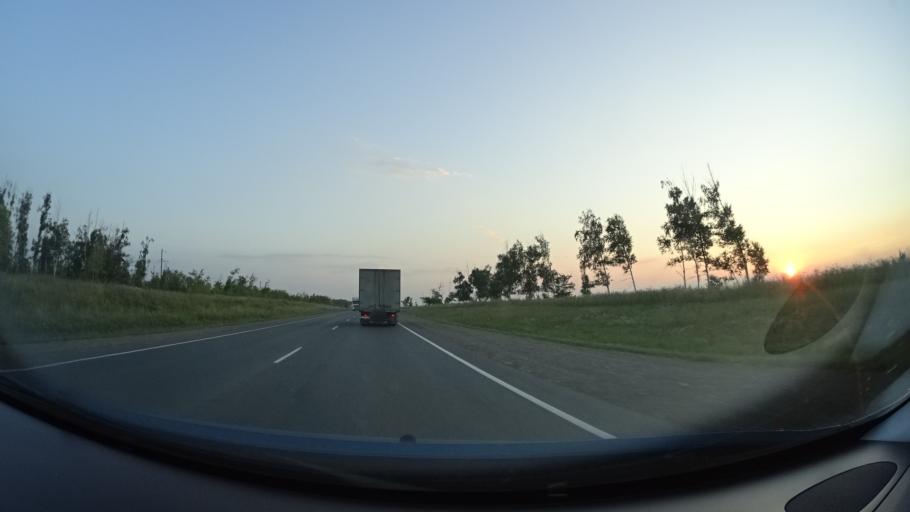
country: RU
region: Samara
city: Sukhodol
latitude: 53.8254
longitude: 51.0622
